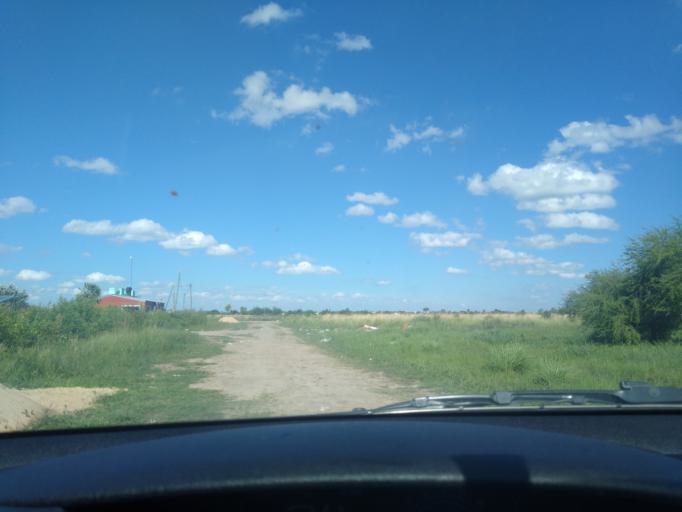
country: AR
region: Chaco
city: Resistencia
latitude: -27.4864
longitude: -59.0130
